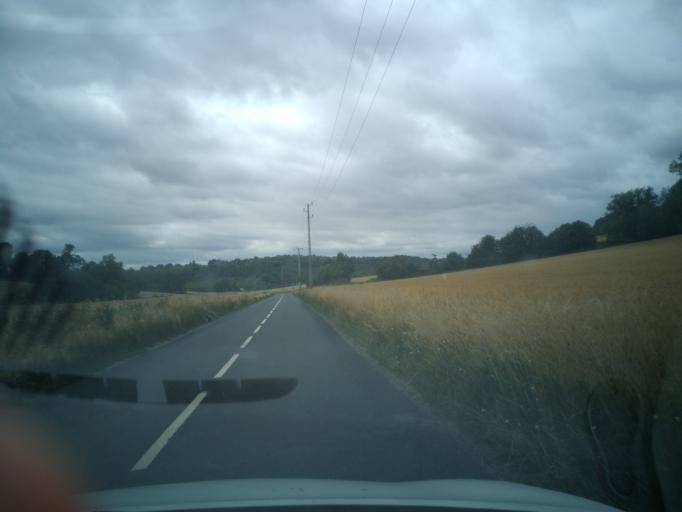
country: FR
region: Ile-de-France
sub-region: Departement des Yvelines
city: Crespieres
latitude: 48.8696
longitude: 1.9168
